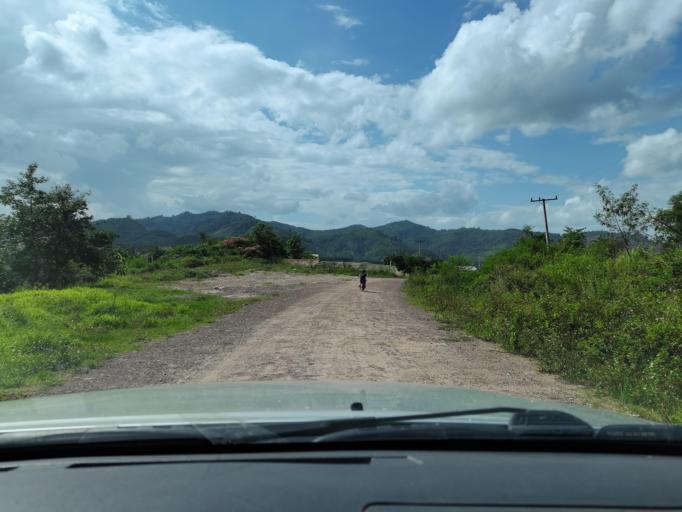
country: LA
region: Loungnamtha
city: Muang Nale
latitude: 20.5900
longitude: 101.0585
